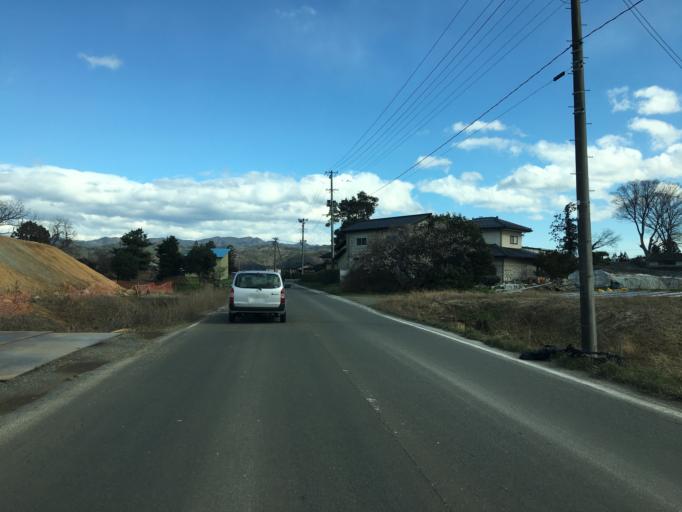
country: JP
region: Fukushima
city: Yanagawamachi-saiwaicho
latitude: 37.8559
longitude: 140.5908
